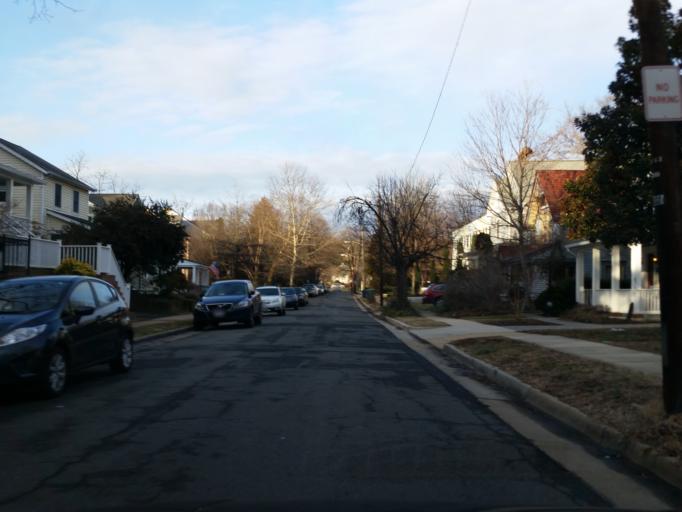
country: US
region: Virginia
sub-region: City of Alexandria
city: Alexandria
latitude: 38.8109
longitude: -77.0586
